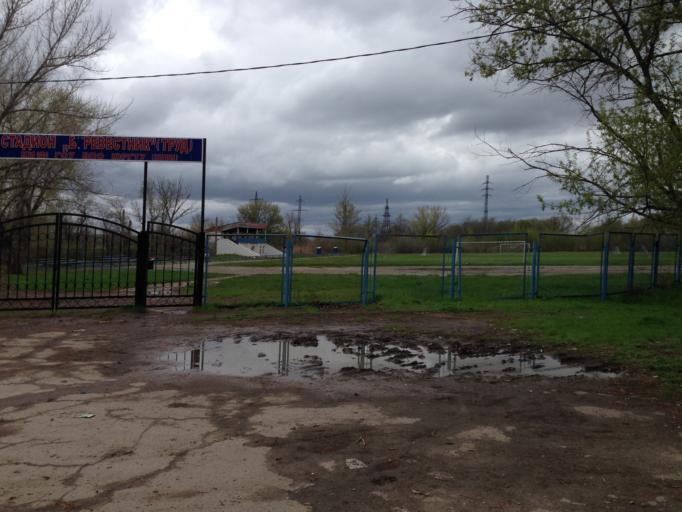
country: RU
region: Rostov
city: Kamensk-Shakhtinskiy
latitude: 48.3326
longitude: 40.2490
